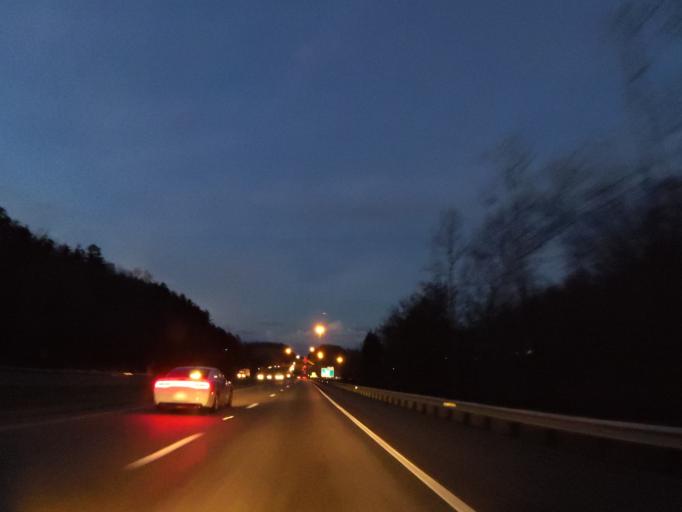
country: US
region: Kentucky
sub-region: Whitley County
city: Corbin
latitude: 36.9097
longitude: -84.1317
